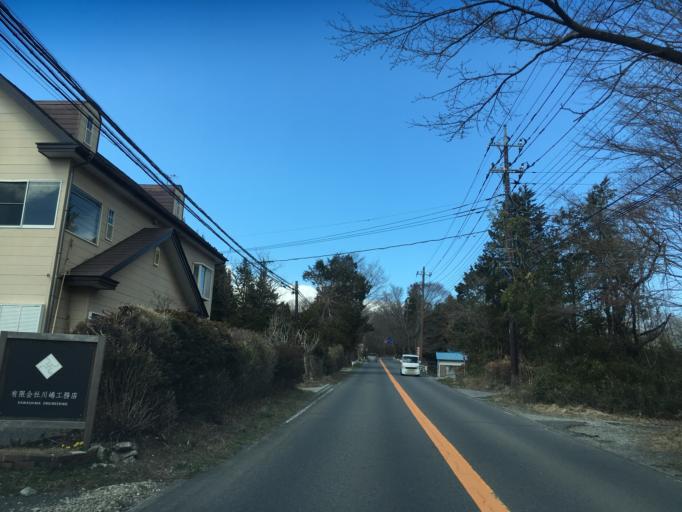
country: JP
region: Tochigi
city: Kuroiso
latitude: 37.0563
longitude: 140.0130
